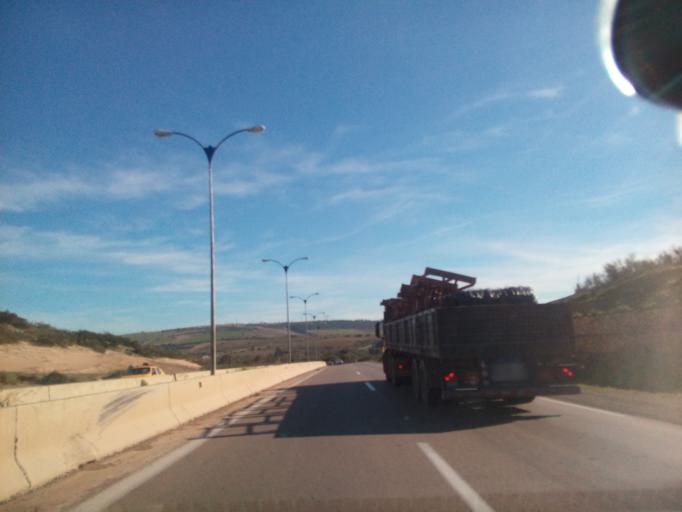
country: DZ
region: Oran
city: Ain el Bya
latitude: 35.7869
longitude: -0.1108
